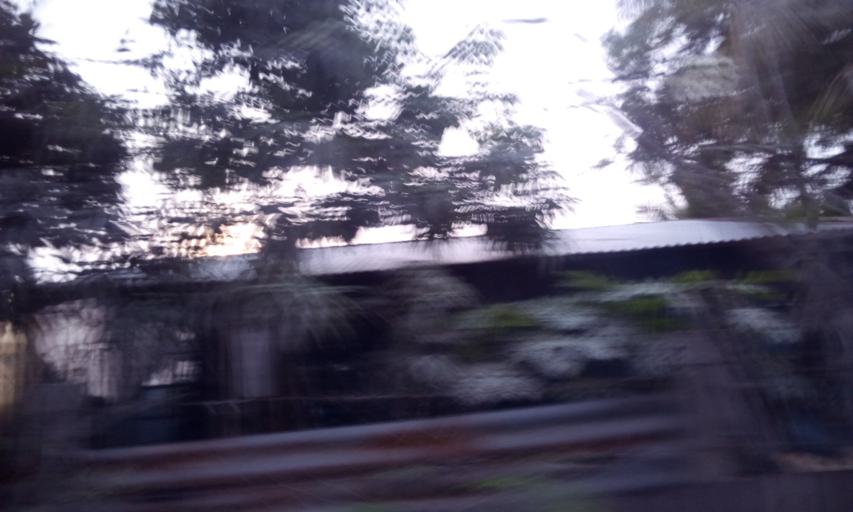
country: TH
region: Bangkok
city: Nong Chok
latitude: 13.8515
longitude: 100.8855
